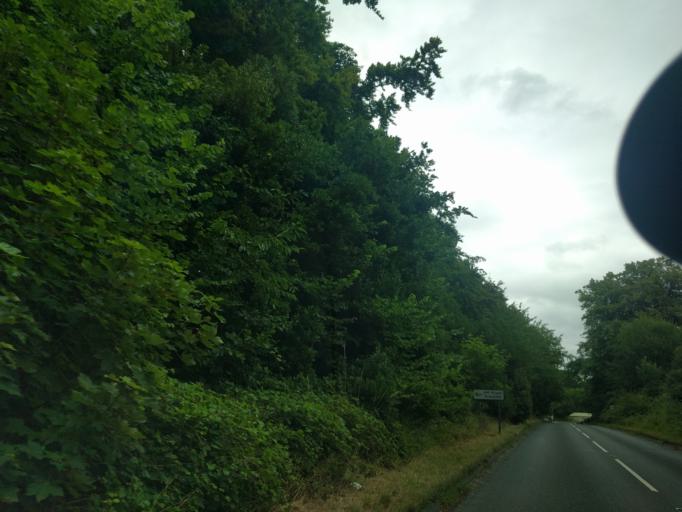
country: GB
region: England
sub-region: Wiltshire
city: Erlestoke
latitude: 51.2830
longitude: -2.0467
